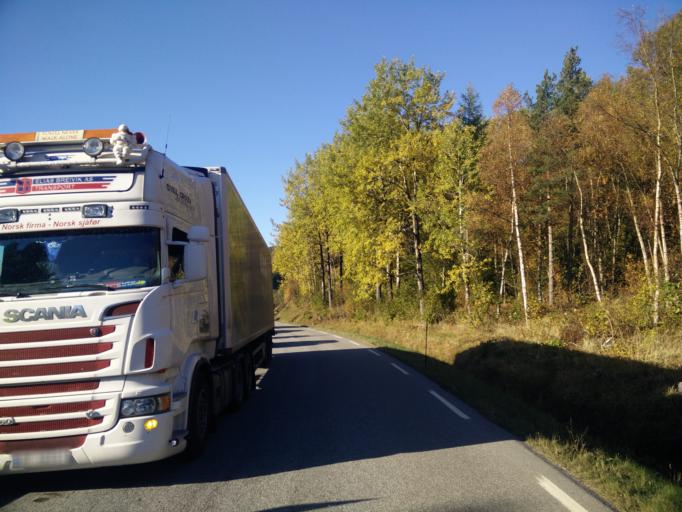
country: NO
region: More og Romsdal
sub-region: Halsa
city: Liaboen
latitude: 63.1130
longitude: 8.3247
